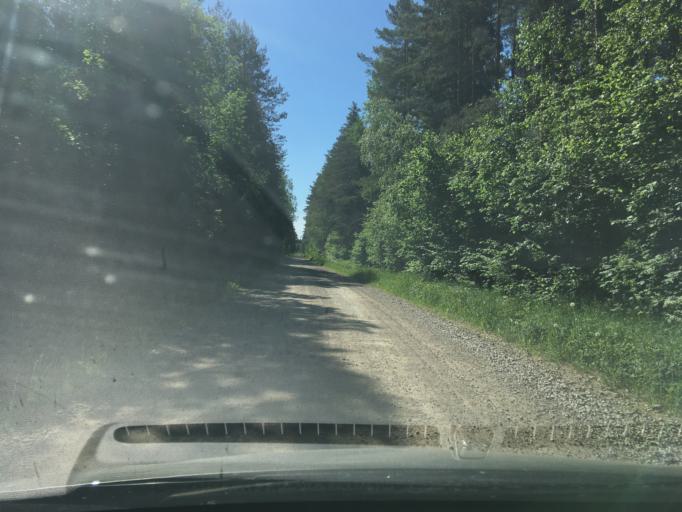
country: EE
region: Laeaene
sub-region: Lihula vald
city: Lihula
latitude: 58.6384
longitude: 23.7920
